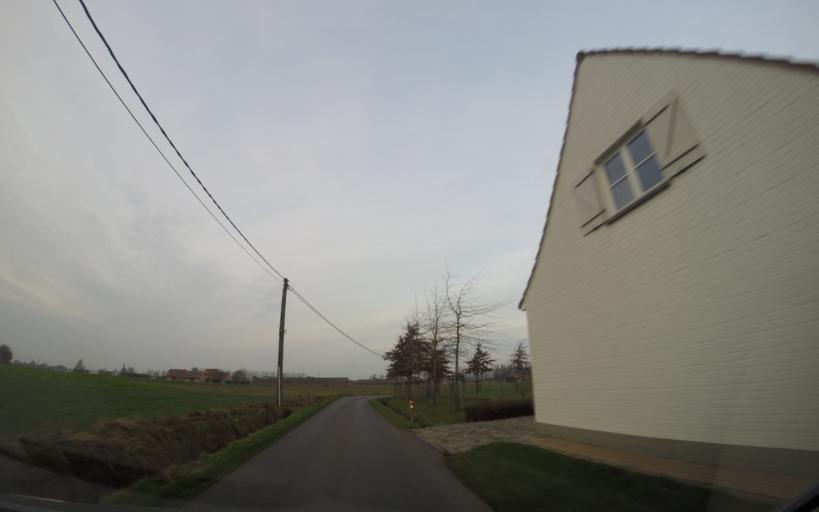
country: BE
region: Flanders
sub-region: Provincie West-Vlaanderen
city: Ruiselede
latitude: 51.0316
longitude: 3.4129
